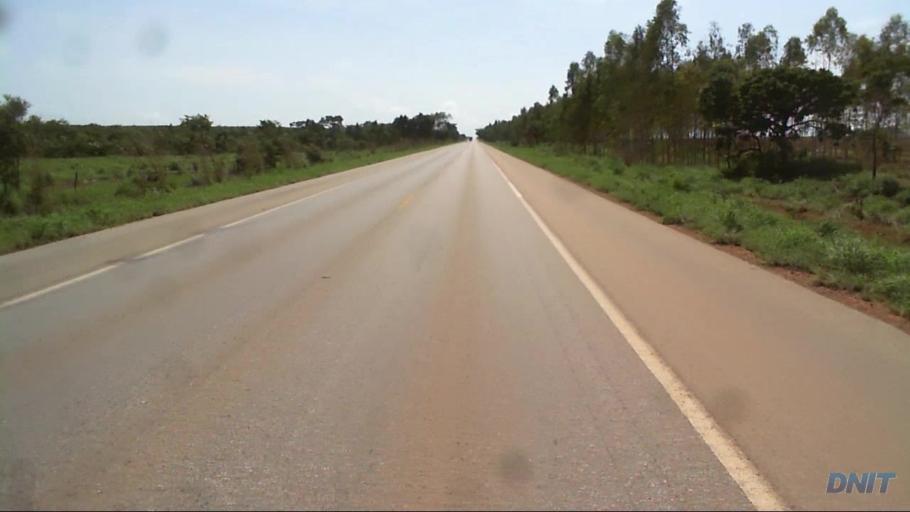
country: BR
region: Goias
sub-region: Barro Alto
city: Barro Alto
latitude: -15.2048
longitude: -48.7324
